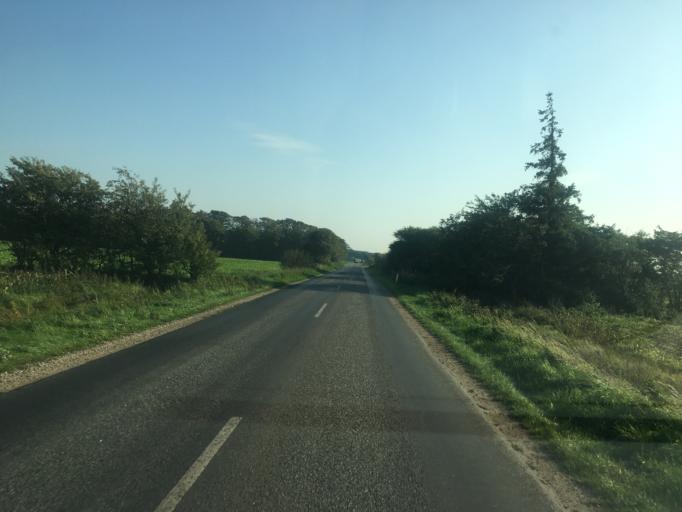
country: DE
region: Schleswig-Holstein
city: Bramstedtlund
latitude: 54.9354
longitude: 9.0673
